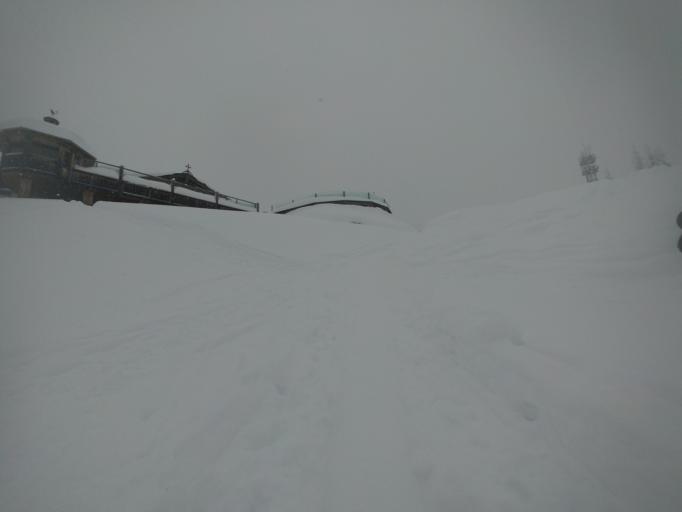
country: AT
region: Salzburg
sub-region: Politischer Bezirk Sankt Johann im Pongau
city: Sankt Johann im Pongau
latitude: 47.3085
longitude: 13.2325
